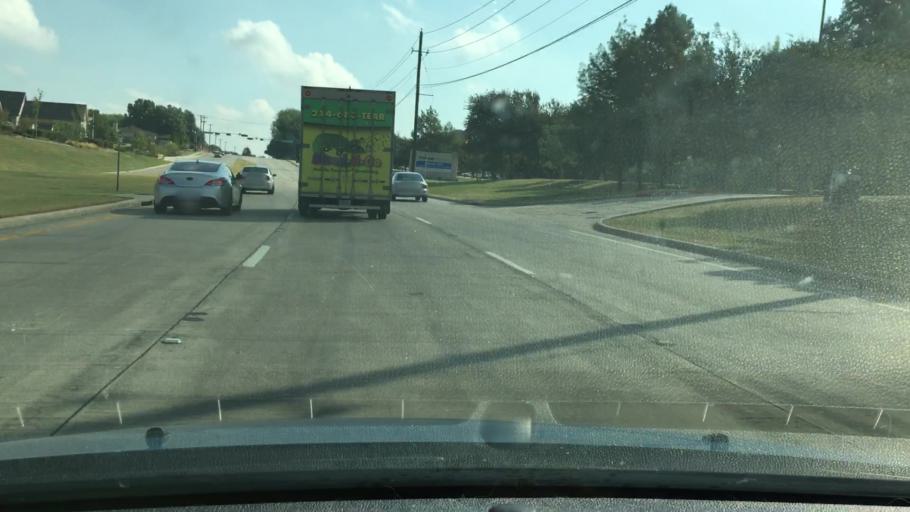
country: US
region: Texas
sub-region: Dallas County
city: Carrollton
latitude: 32.9849
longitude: -96.8639
